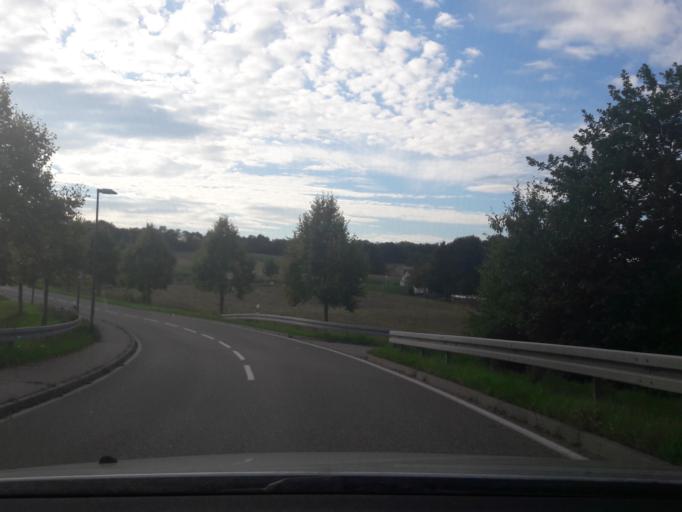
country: DE
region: Baden-Wuerttemberg
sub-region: Regierungsbezirk Stuttgart
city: Abstatt
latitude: 49.0802
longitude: 9.2944
